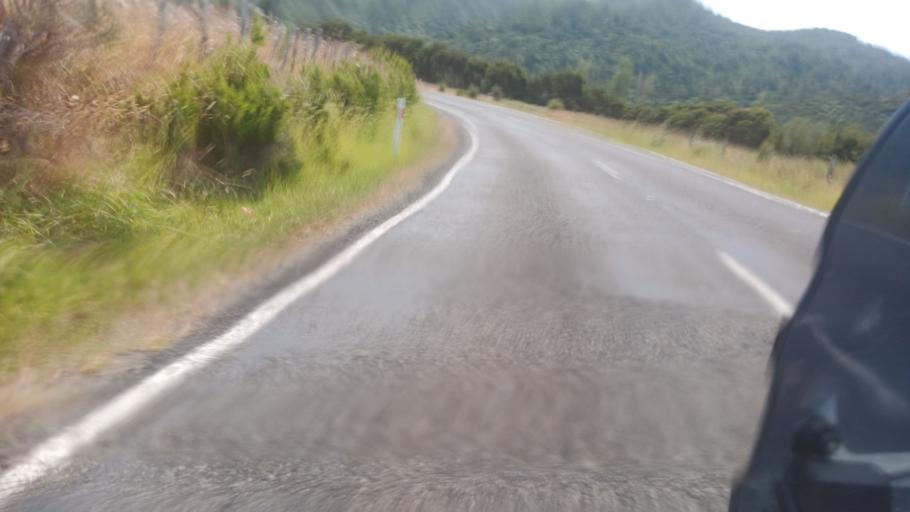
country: NZ
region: Bay of Plenty
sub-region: Opotiki District
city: Opotiki
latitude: -37.5748
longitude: 178.1465
